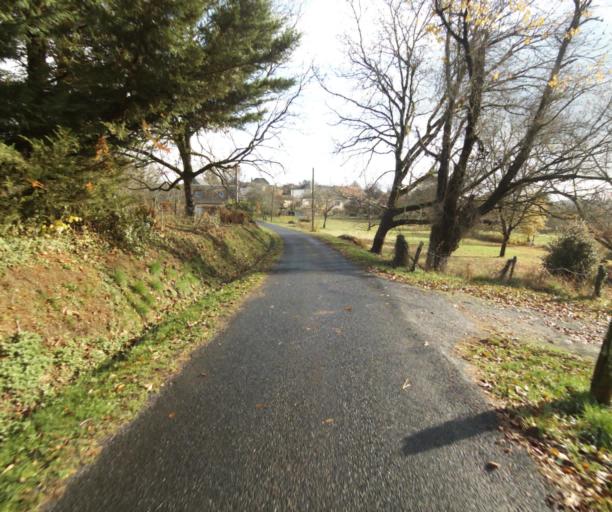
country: FR
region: Limousin
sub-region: Departement de la Correze
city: Cornil
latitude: 45.2250
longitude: 1.6865
